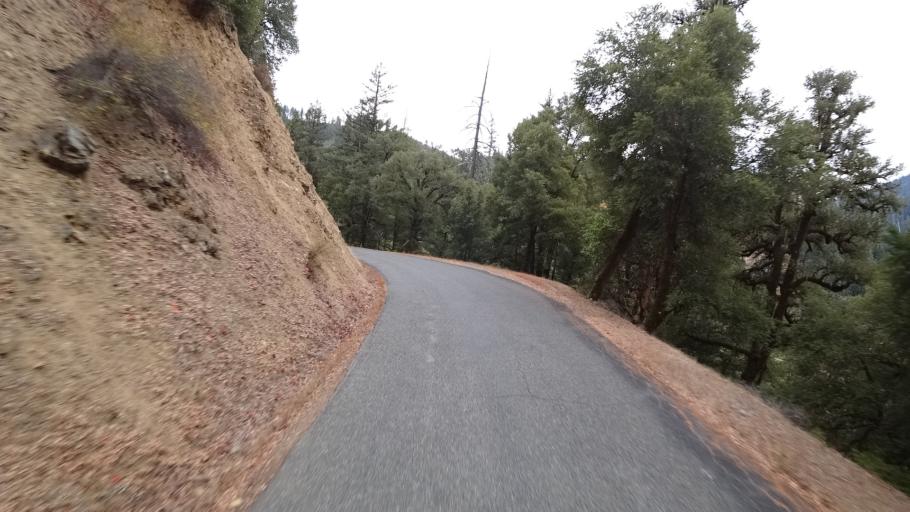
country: US
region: California
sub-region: Siskiyou County
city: Happy Camp
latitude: 41.7583
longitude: -123.3609
